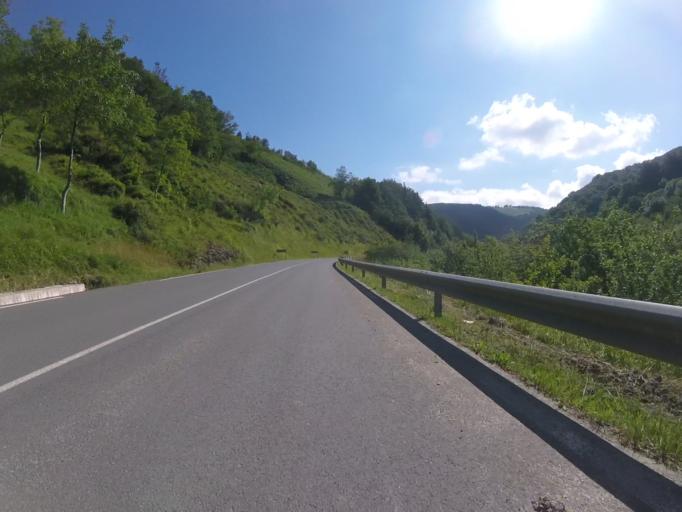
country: ES
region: Basque Country
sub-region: Provincia de Guipuzcoa
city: Beizama
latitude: 43.1131
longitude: -2.2330
